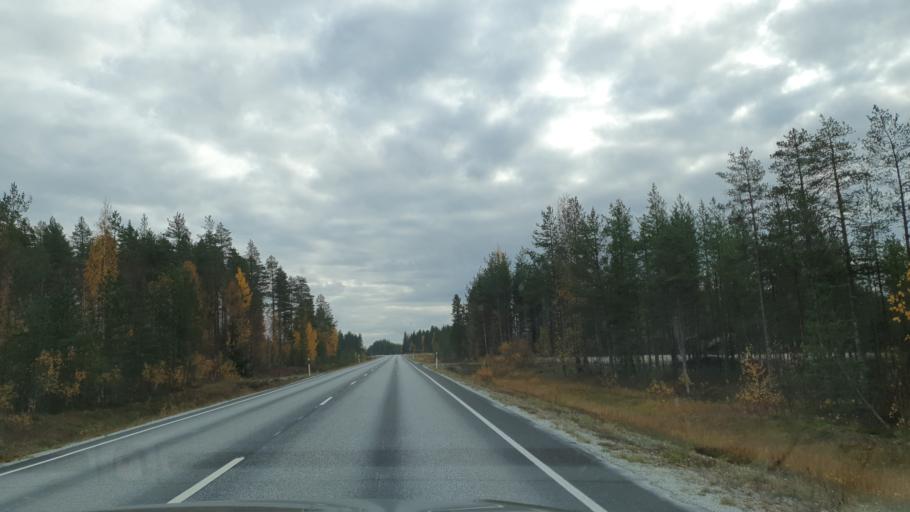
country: FI
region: Northern Ostrobothnia
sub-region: Oulunkaari
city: Pudasjaervi
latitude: 65.4196
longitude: 26.8746
